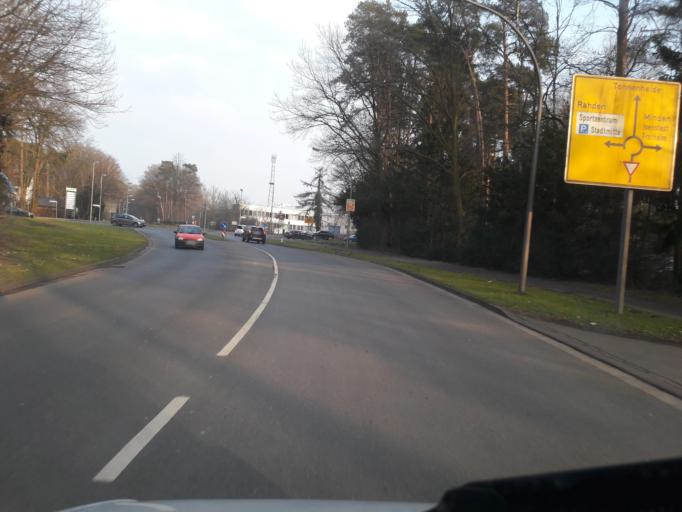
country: DE
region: North Rhine-Westphalia
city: Espelkamp
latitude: 52.3720
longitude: 8.6342
